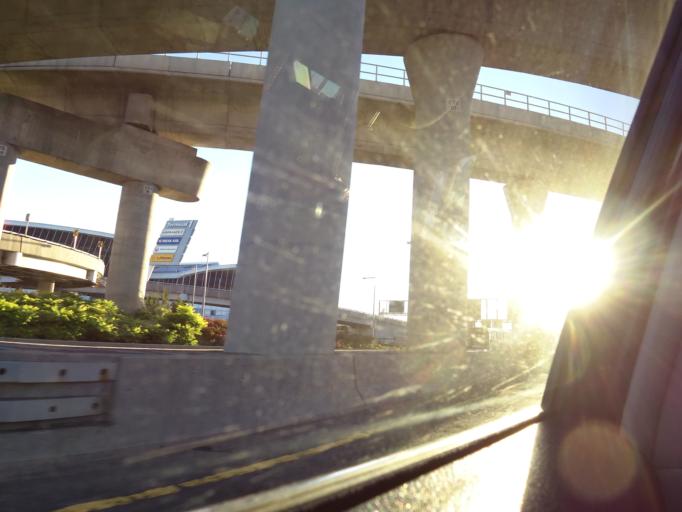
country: US
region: New York
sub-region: Nassau County
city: Inwood
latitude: 40.6449
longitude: -73.7901
